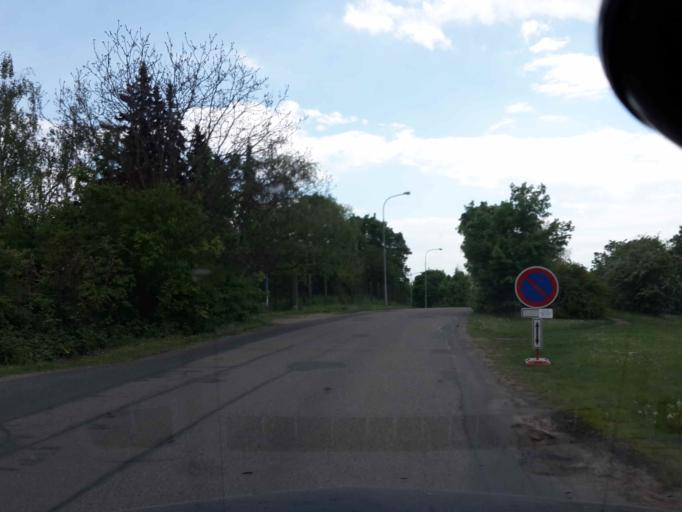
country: CZ
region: South Moravian
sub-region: Mesto Brno
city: Brno
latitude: 49.2277
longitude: 16.6317
